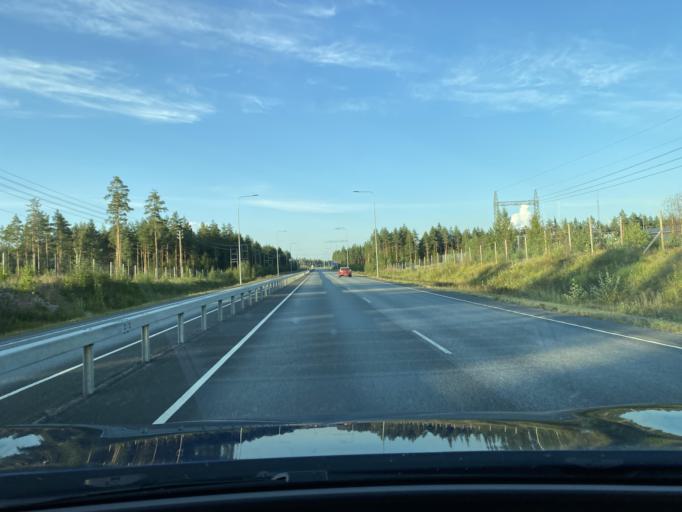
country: FI
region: Southern Ostrobothnia
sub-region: Seinaejoki
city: Seinaejoki
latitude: 62.7275
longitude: 22.8842
